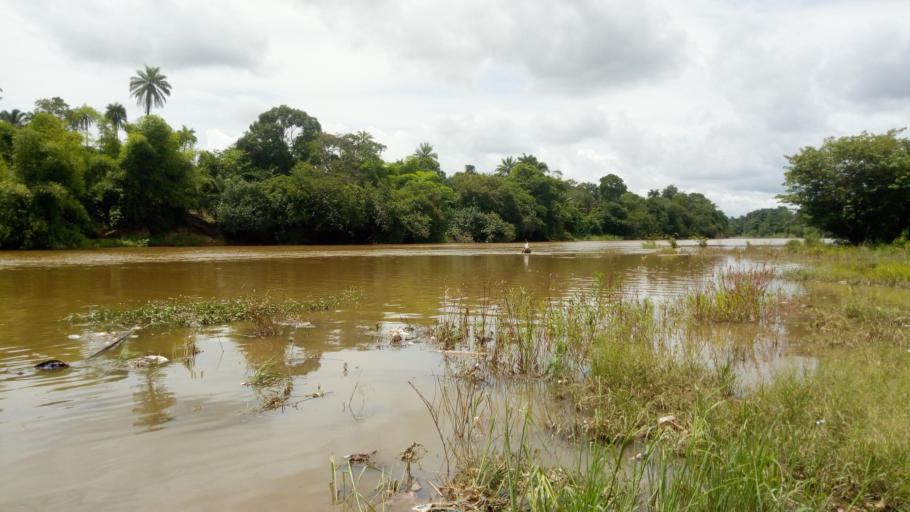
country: SL
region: Northern Province
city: Magburaka
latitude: 8.7246
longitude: -11.9547
